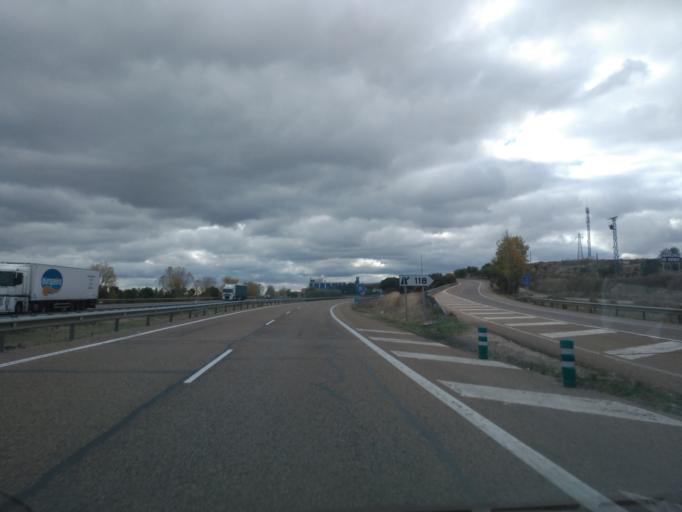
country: ES
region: Castille and Leon
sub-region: Provincia de Valladolid
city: Santovenia de Pisuerga
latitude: 41.7050
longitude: -4.7095
